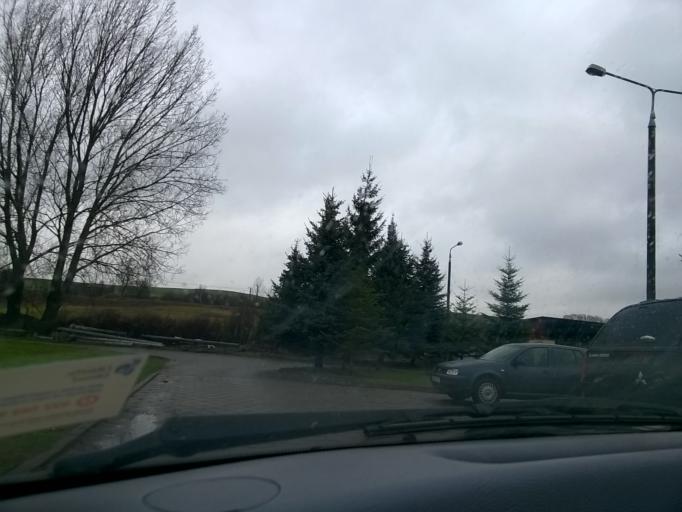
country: PL
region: Kujawsko-Pomorskie
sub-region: Powiat nakielski
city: Naklo nad Notecia
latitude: 53.1324
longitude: 17.5422
